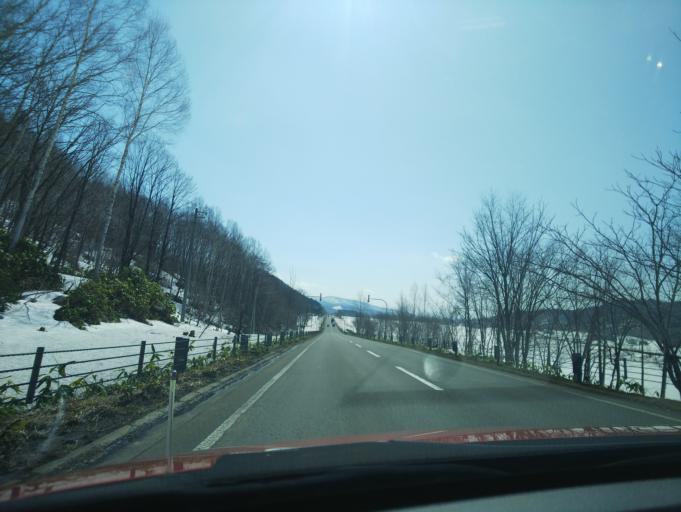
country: JP
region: Hokkaido
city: Nayoro
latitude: 44.6355
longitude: 142.2772
